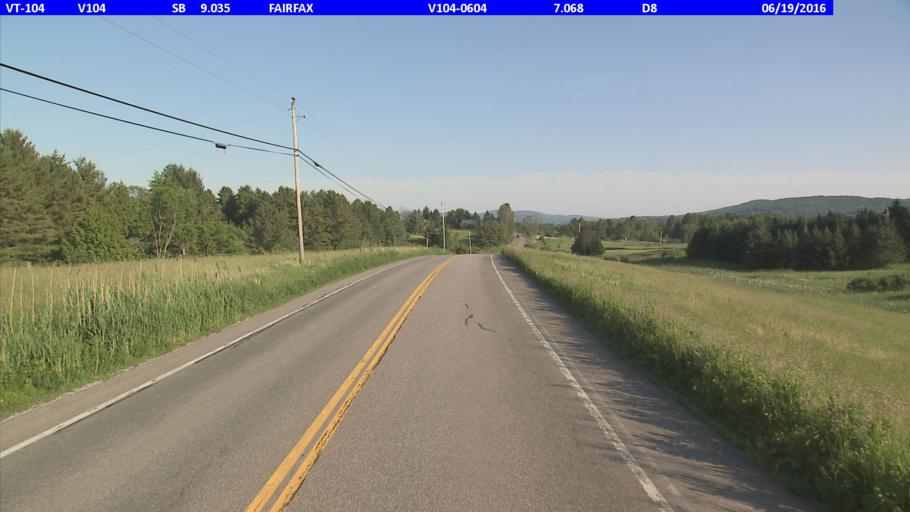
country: US
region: Vermont
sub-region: Chittenden County
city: Milton
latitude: 44.6871
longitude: -73.0313
